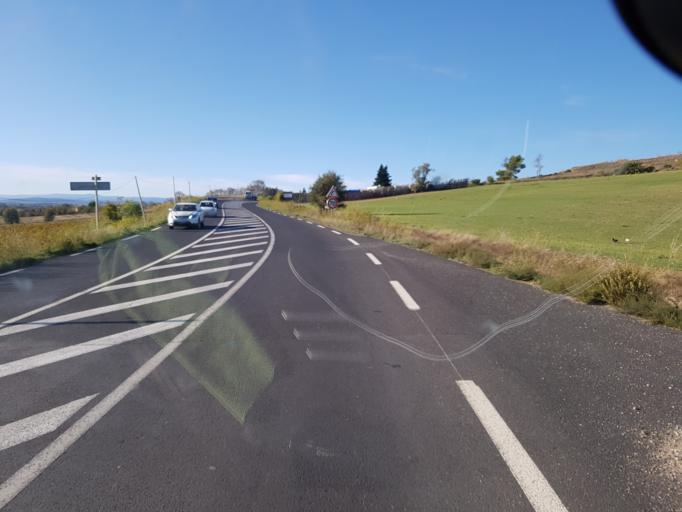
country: FR
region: Languedoc-Roussillon
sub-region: Departement de l'Aude
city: Coursan
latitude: 43.2704
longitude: 3.0799
